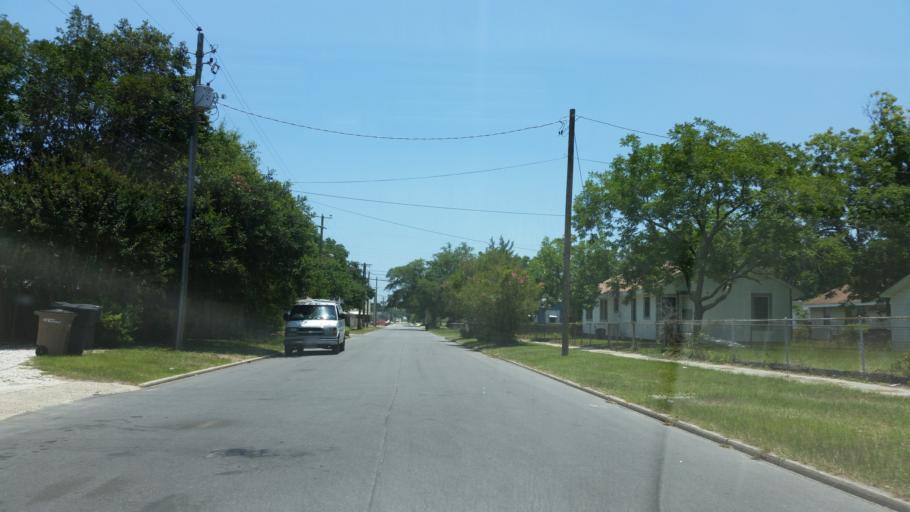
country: US
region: Florida
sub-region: Escambia County
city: Pensacola
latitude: 30.4095
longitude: -87.2352
